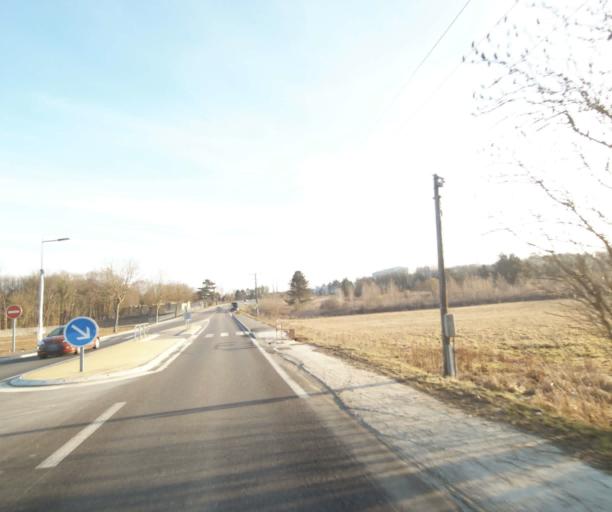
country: FR
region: Lorraine
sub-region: Departement de Meurthe-et-Moselle
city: Chavigny
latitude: 48.6432
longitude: 6.1356
